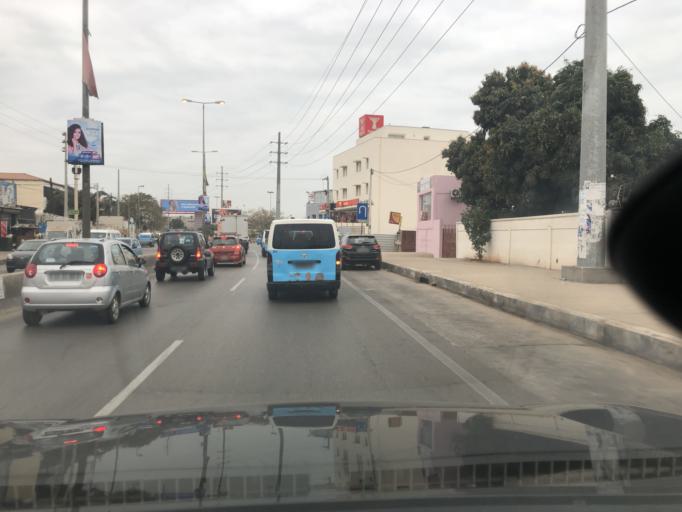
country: AO
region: Luanda
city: Luanda
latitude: -8.8938
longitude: 13.1833
